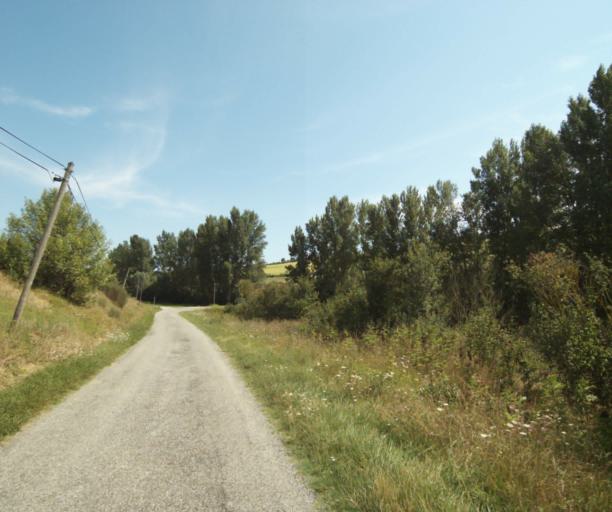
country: FR
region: Midi-Pyrenees
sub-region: Departement de l'Ariege
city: Lezat-sur-Leze
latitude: 43.2451
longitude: 1.4027
